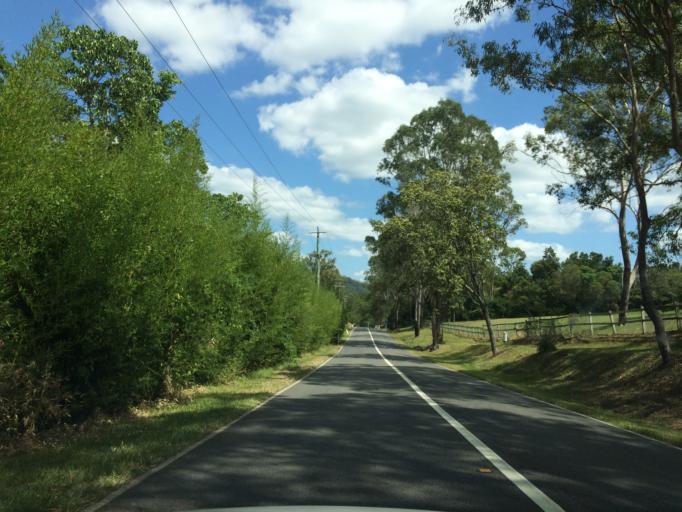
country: AU
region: Queensland
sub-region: Brisbane
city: Kenmore Hills
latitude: -27.4964
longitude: 152.9239
